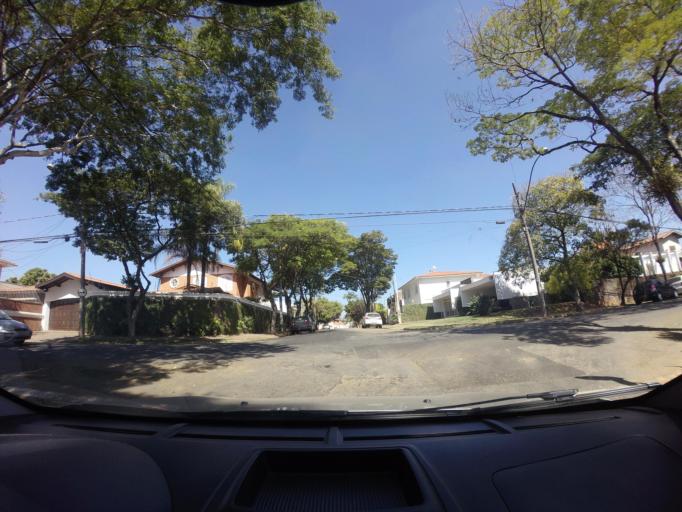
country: BR
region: Sao Paulo
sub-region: Piracicaba
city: Piracicaba
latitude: -22.7136
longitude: -47.6381
